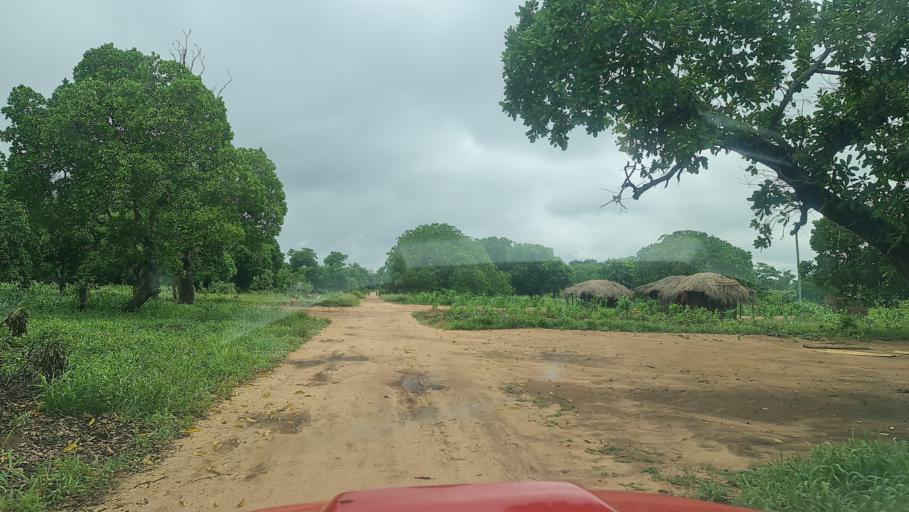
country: MW
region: Southern Region
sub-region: Nsanje District
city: Nsanje
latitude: -17.1789
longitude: 35.8972
